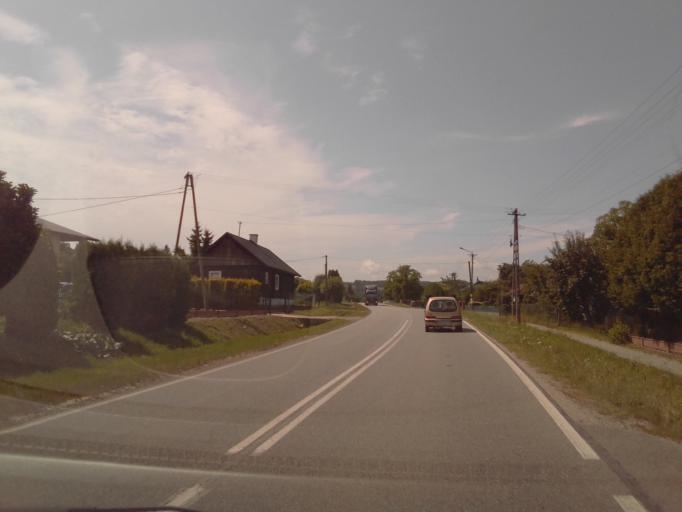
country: PL
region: Subcarpathian Voivodeship
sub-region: Powiat ropczycko-sedziszowski
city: Ropczyce
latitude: 50.0370
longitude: 21.5797
